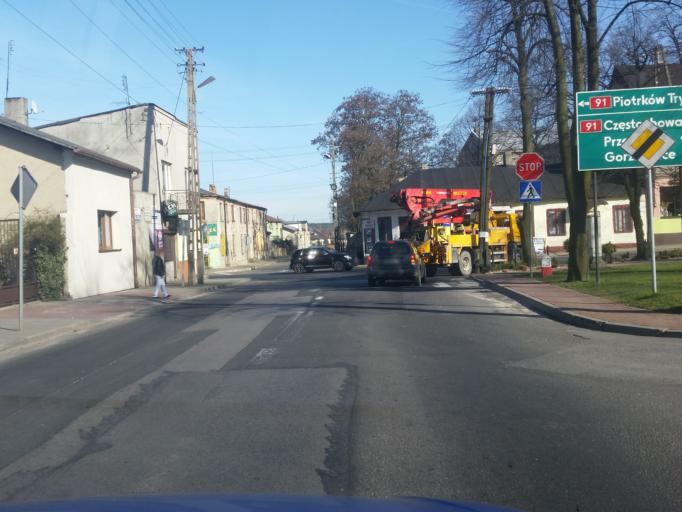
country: PL
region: Lodz Voivodeship
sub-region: Powiat radomszczanski
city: Kamiensk
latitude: 51.2049
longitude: 19.4981
